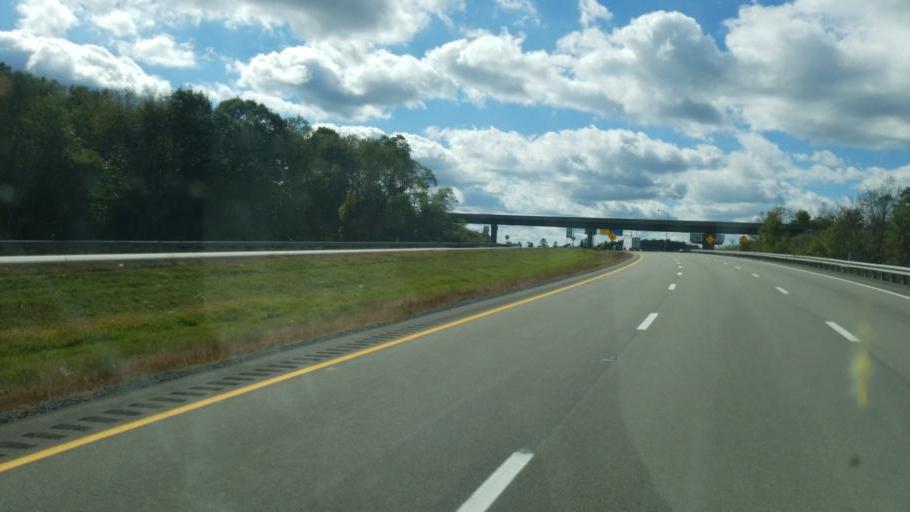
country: US
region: West Virginia
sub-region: Preston County
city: Terra Alta
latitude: 39.6633
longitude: -79.4869
